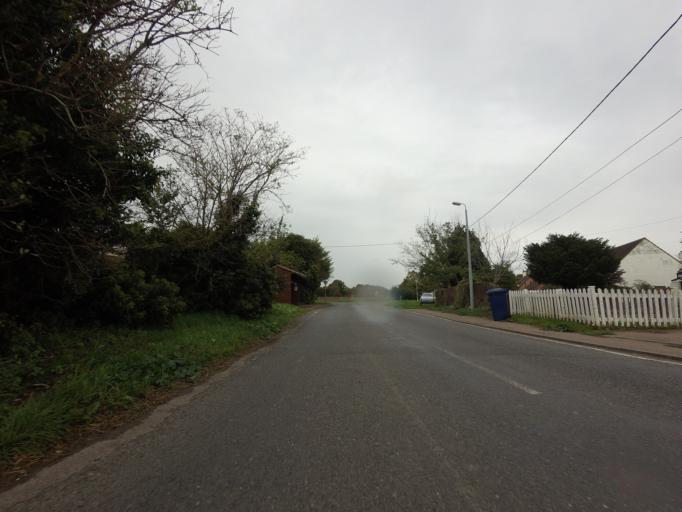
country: GB
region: England
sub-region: Cambridgeshire
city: Harston
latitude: 52.0873
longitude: 0.0746
